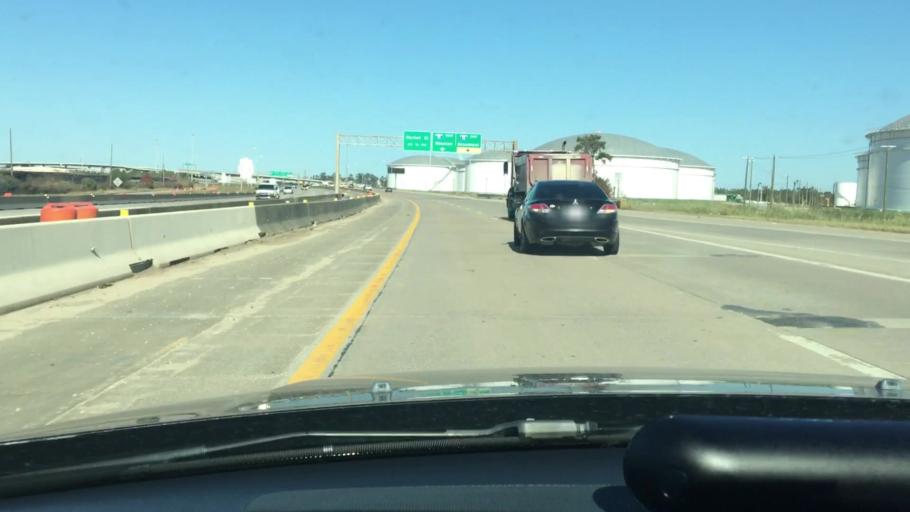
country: US
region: Texas
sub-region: Harris County
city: Cloverleaf
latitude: 29.7592
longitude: -95.1461
